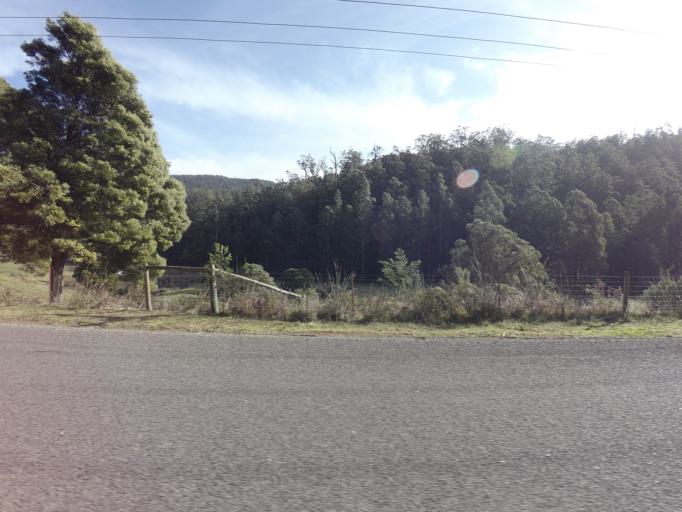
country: AU
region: Tasmania
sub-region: Huon Valley
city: Huonville
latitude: -43.0434
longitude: 147.1243
